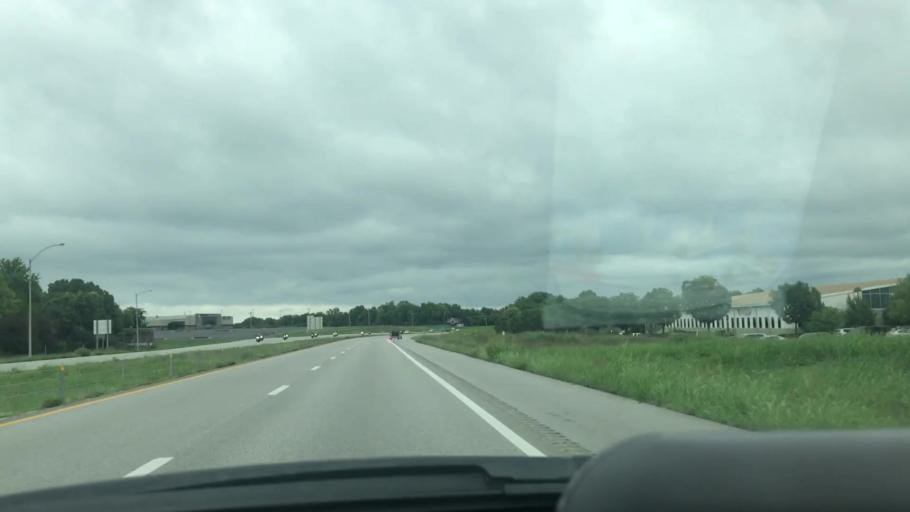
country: US
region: Missouri
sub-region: Greene County
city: Springfield
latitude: 37.2464
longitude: -93.3477
